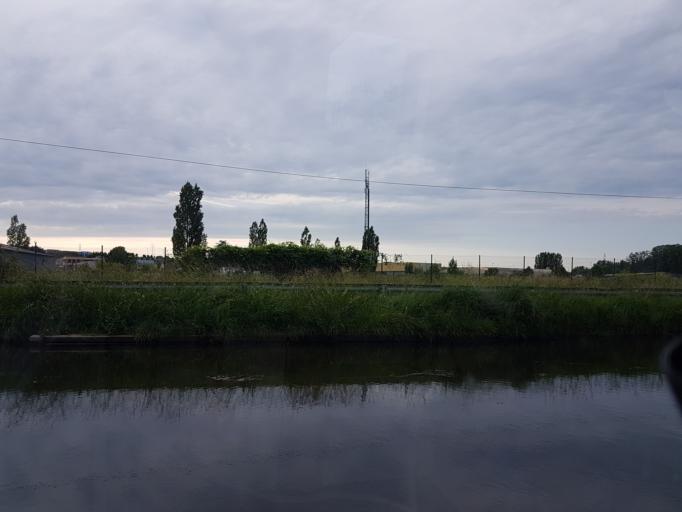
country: FR
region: Bourgogne
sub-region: Departement de l'Yonne
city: Auxerre
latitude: 47.8141
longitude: 3.5798
